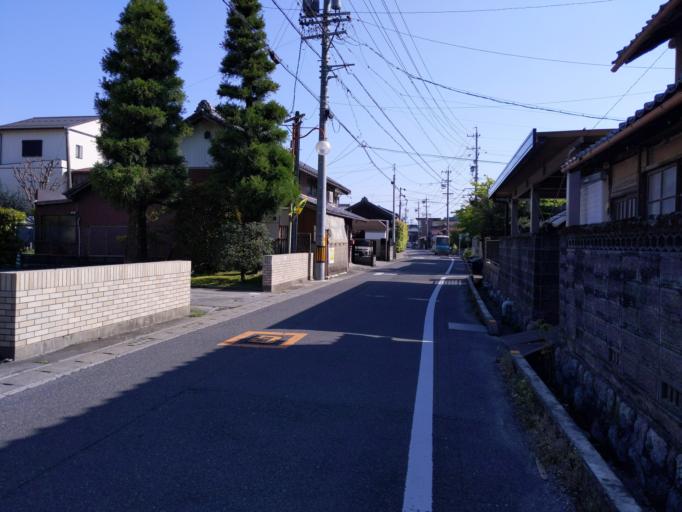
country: JP
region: Gifu
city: Godo
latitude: 35.3932
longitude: 136.5817
